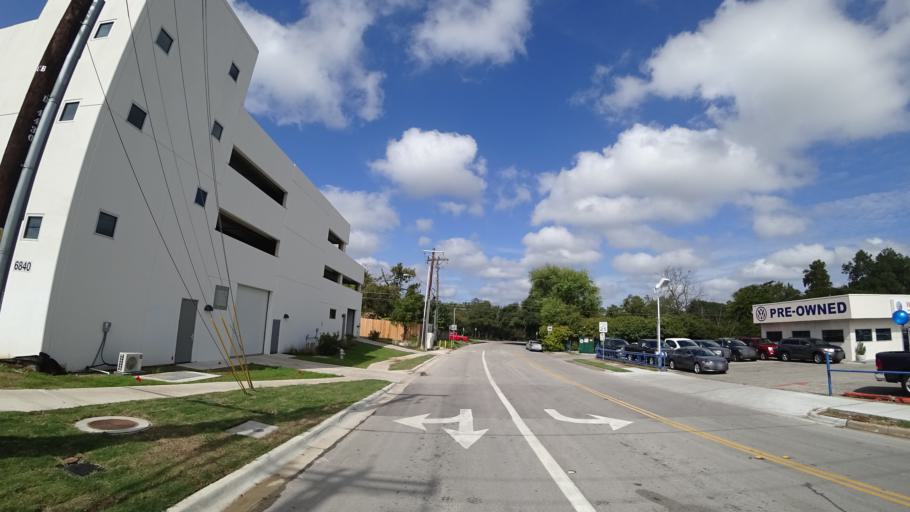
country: US
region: Texas
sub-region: Travis County
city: Austin
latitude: 30.3455
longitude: -97.7376
